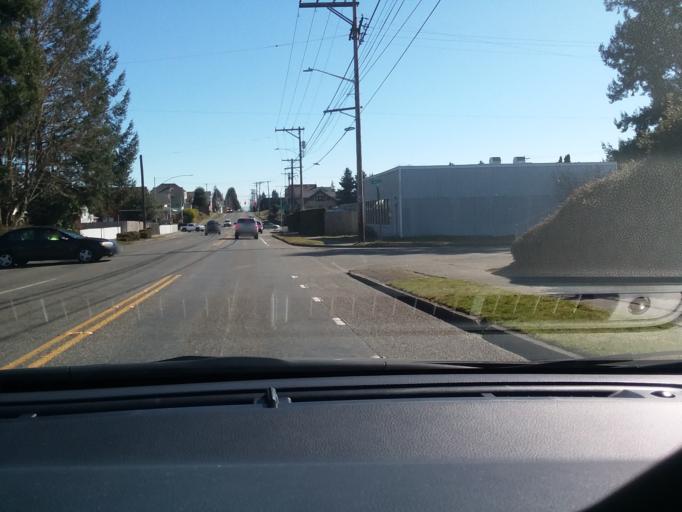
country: US
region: Washington
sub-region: Pierce County
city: Tacoma
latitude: 47.2500
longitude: -122.4781
